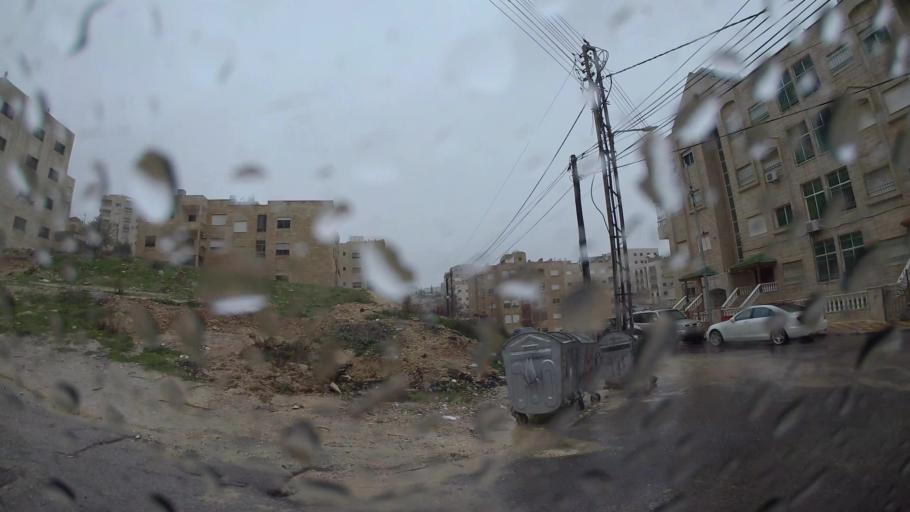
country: JO
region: Amman
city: Al Jubayhah
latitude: 32.0122
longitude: 35.8924
